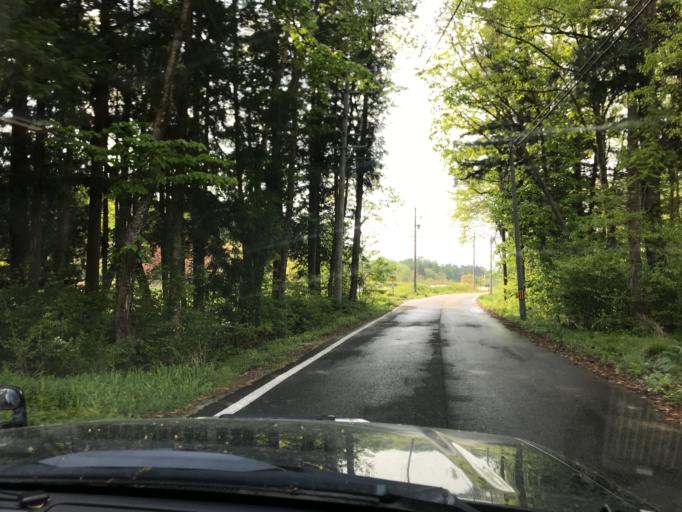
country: JP
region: Nagano
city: Omachi
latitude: 36.5211
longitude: 137.8125
